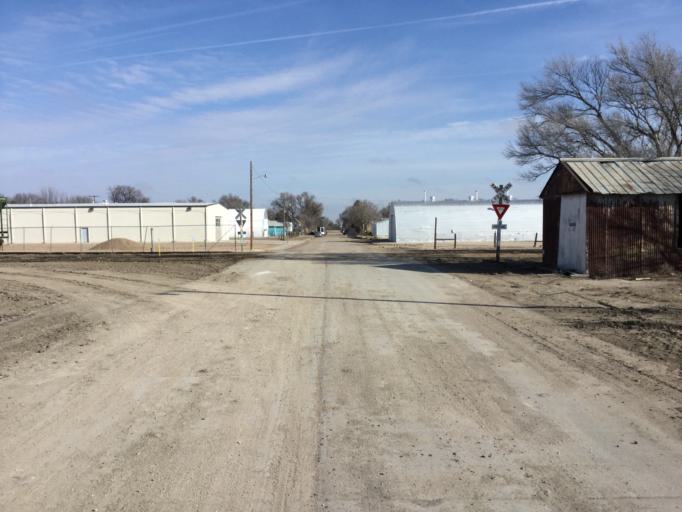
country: US
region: Kansas
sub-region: Scott County
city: Scott City
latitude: 38.4875
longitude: -100.9044
